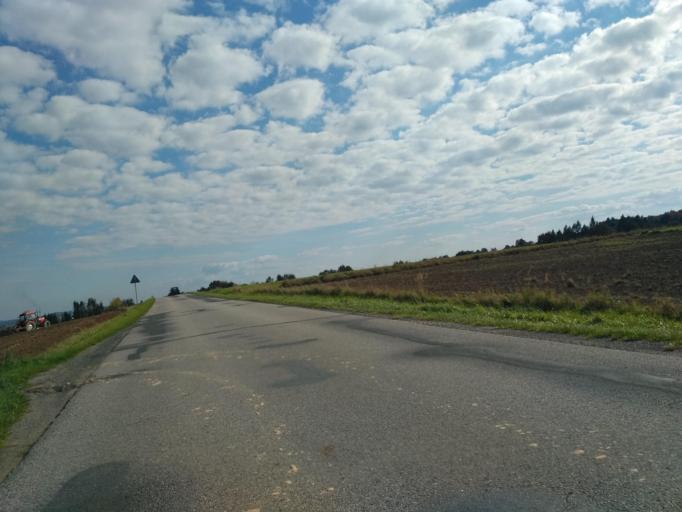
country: PL
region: Subcarpathian Voivodeship
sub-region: Powiat debicki
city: Brzostek
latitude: 49.8909
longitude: 21.3488
